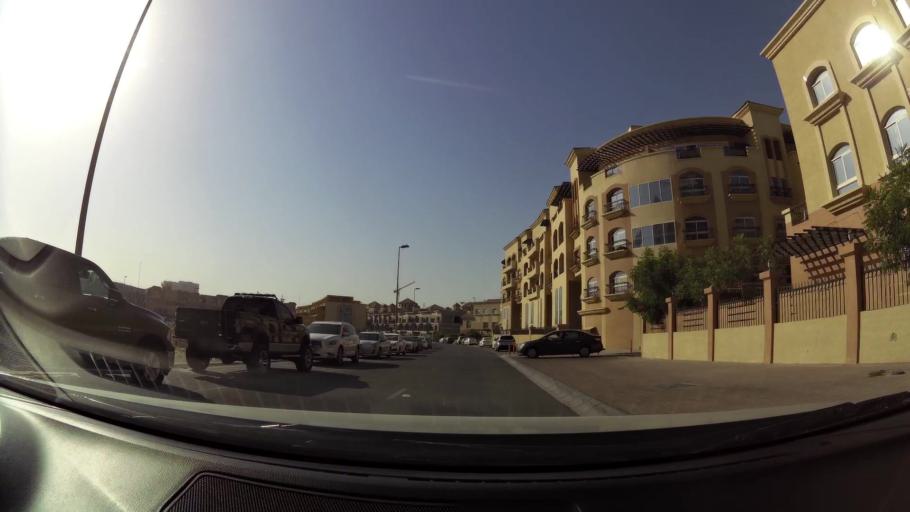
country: AE
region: Dubai
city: Dubai
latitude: 25.0614
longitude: 55.2174
